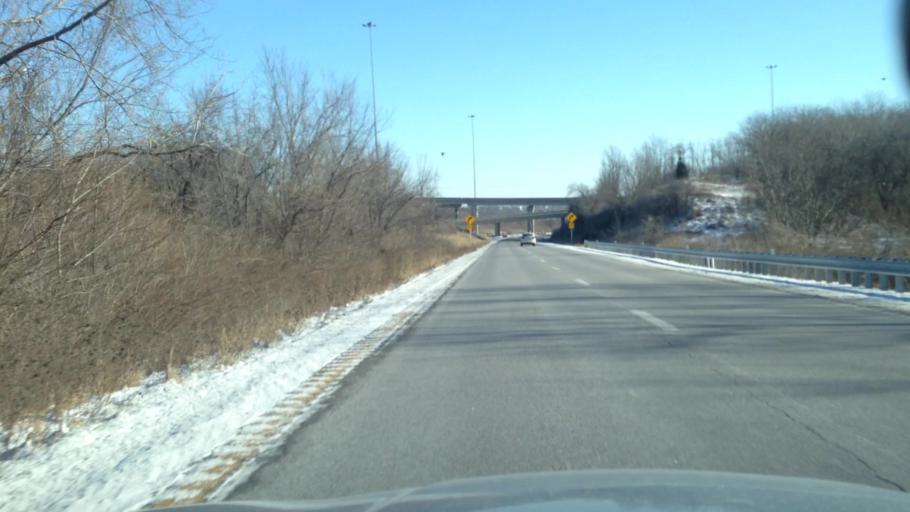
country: US
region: Missouri
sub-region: Platte County
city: Riverside
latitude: 39.1888
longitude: -94.6174
